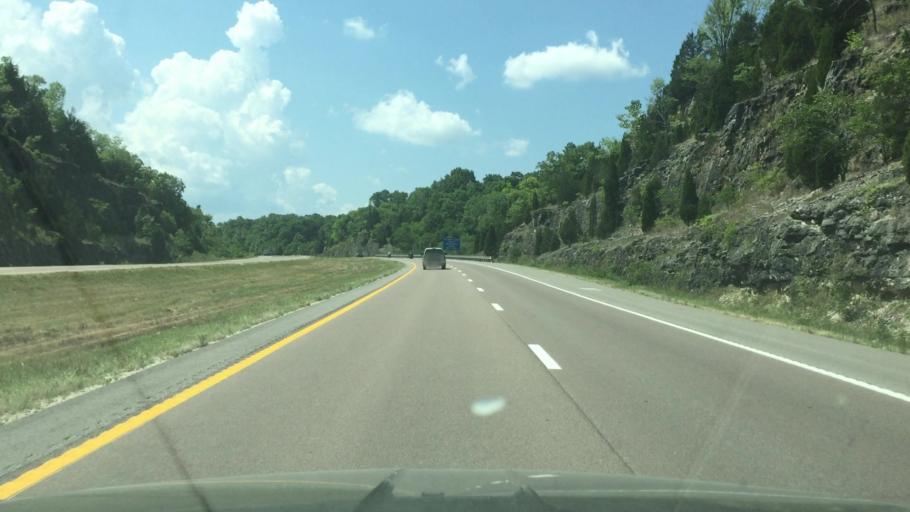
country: US
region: Missouri
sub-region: Miller County
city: Lake Ozark
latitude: 38.2249
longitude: -92.6253
